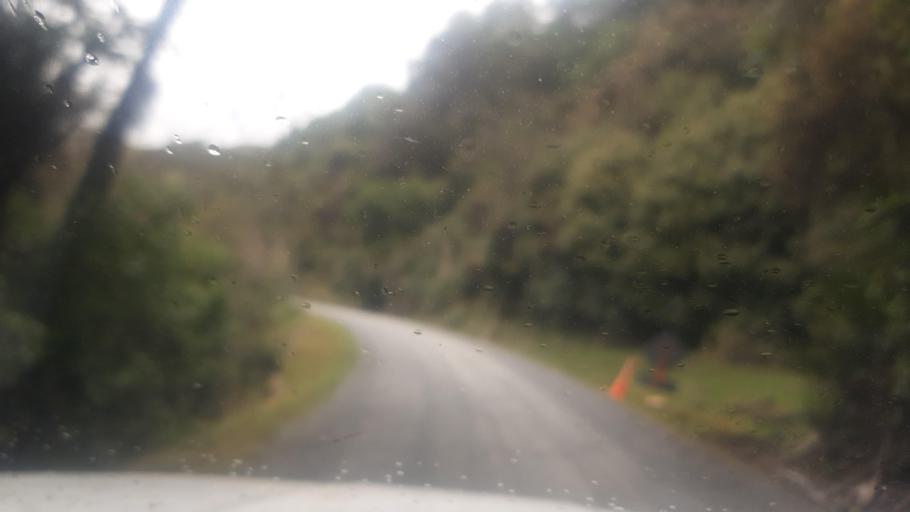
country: NZ
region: Northland
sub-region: Far North District
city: Taipa
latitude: -35.0953
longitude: 173.3947
